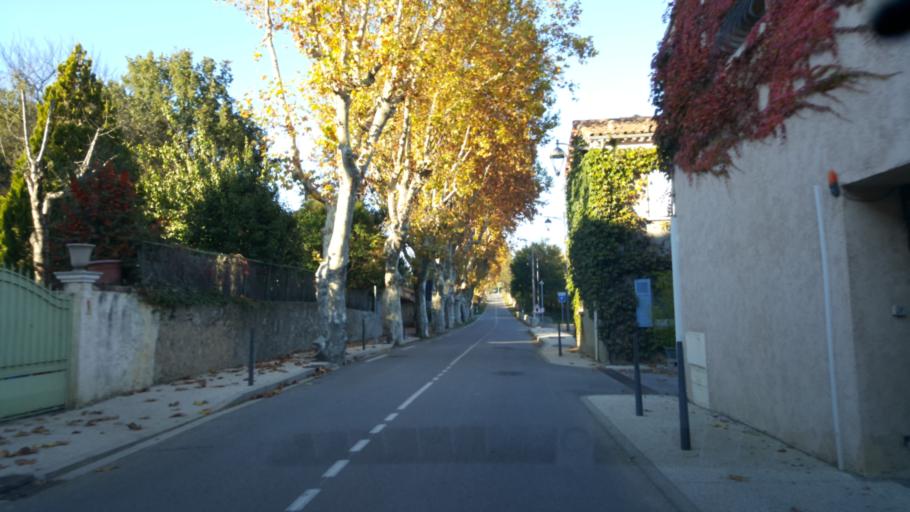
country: FR
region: Provence-Alpes-Cote d'Azur
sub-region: Departement du Var
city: Bras
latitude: 43.5280
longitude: 5.9460
